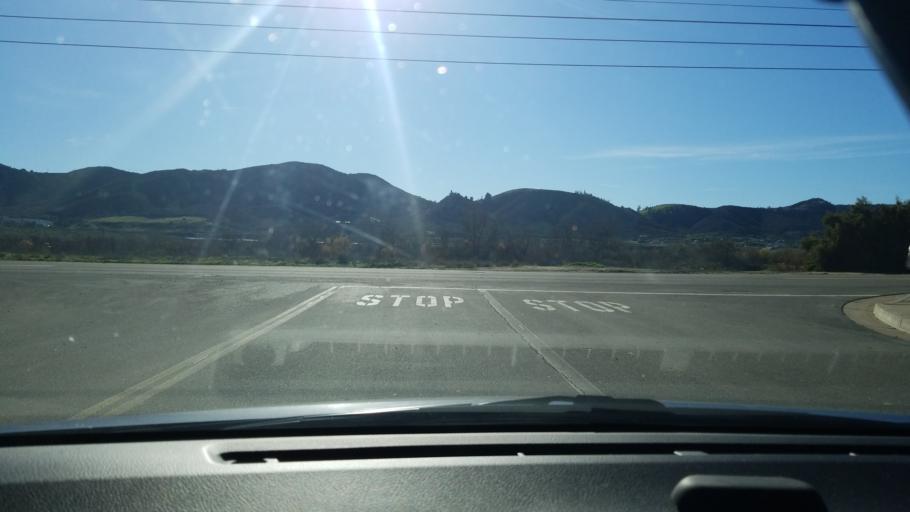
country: US
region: California
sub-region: Riverside County
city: Murrieta Hot Springs
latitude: 33.5289
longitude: -117.1807
